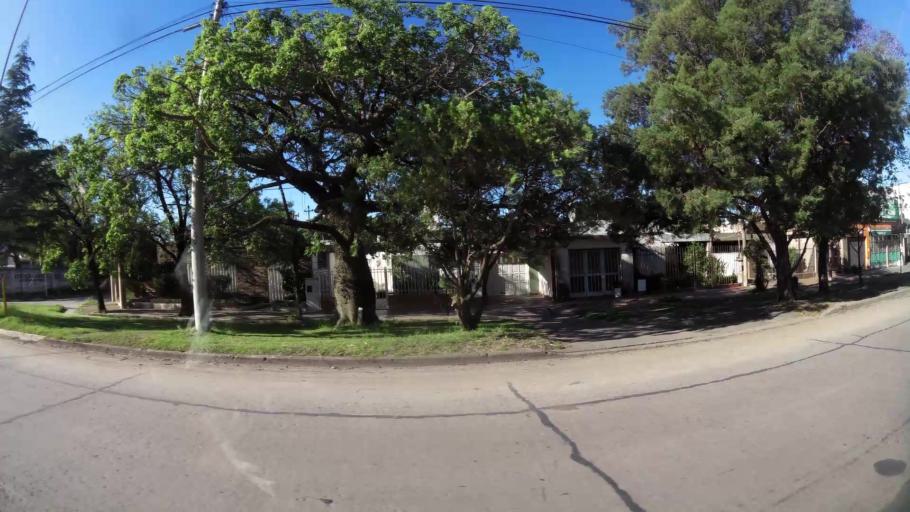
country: AR
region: Cordoba
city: San Francisco
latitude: -31.4174
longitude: -62.0784
